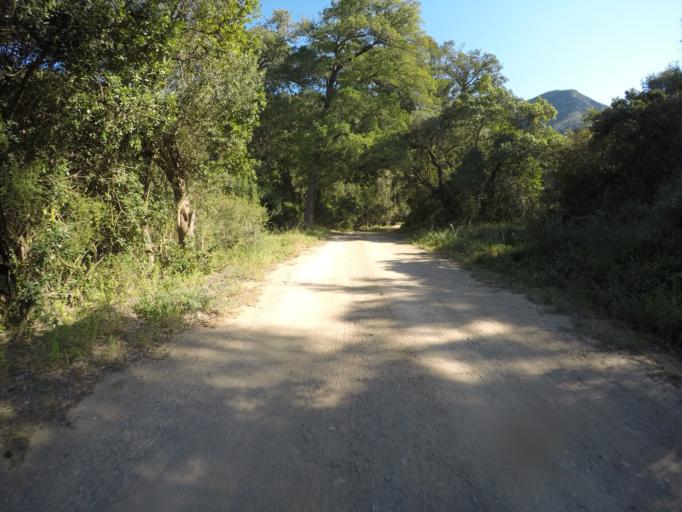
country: ZA
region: Eastern Cape
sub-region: Cacadu District Municipality
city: Kareedouw
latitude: -33.6567
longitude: 24.5237
